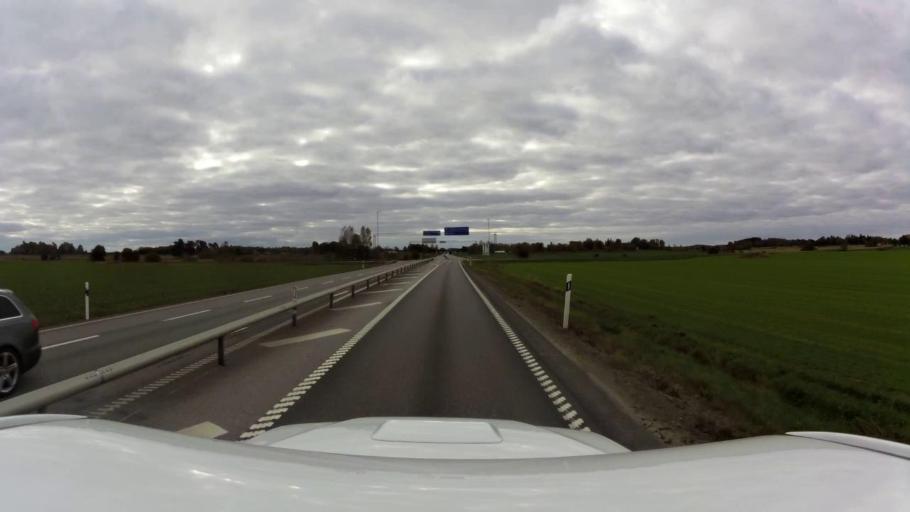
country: SE
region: OEstergoetland
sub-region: Linkopings Kommun
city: Malmslatt
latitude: 58.3522
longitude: 15.5483
